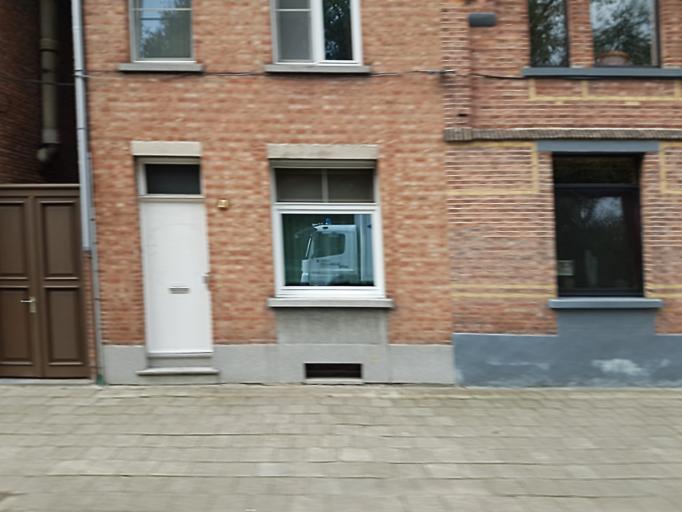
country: BE
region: Flanders
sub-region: Provincie Antwerpen
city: Zwijndrecht
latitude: 51.2064
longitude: 4.3506
